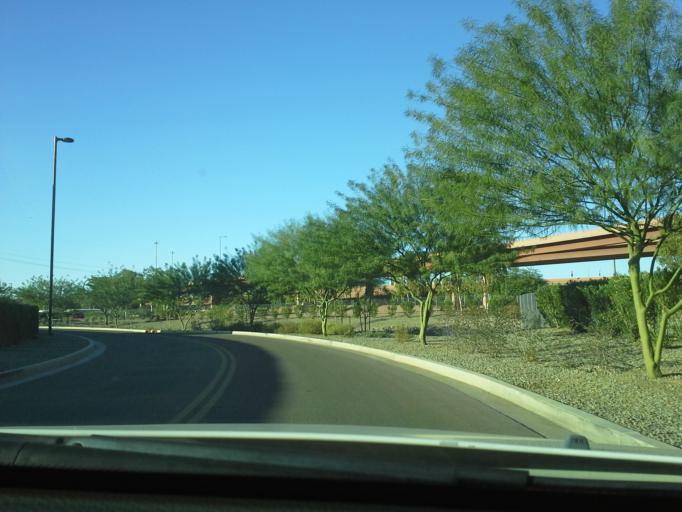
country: US
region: Arizona
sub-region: Maricopa County
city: Tempe
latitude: 33.4318
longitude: -111.8884
